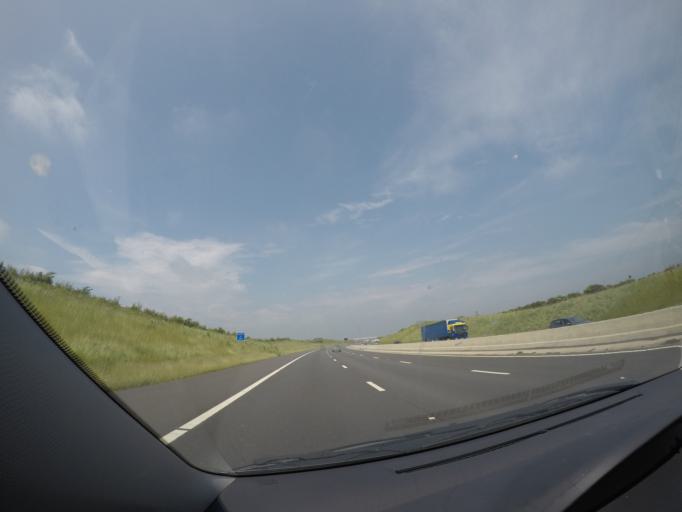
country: GB
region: England
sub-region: North Yorkshire
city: Catterick
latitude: 54.3652
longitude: -1.6321
